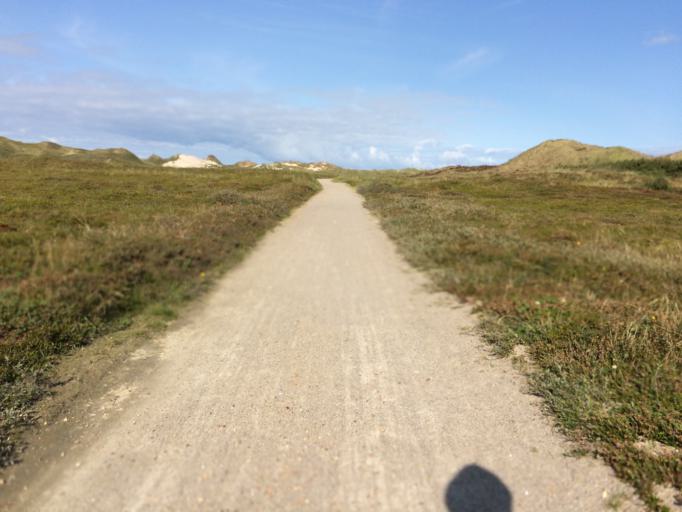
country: DK
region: Central Jutland
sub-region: Ringkobing-Skjern Kommune
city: Hvide Sande
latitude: 55.9170
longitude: 8.1618
